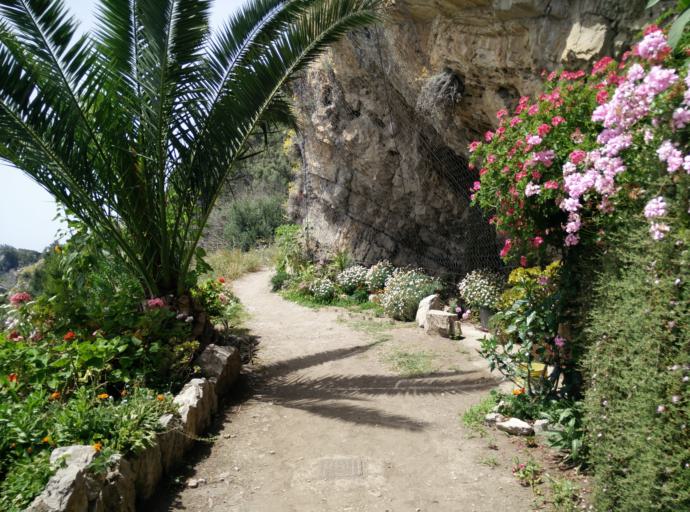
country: IT
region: Campania
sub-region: Provincia di Napoli
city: Massa Lubrense
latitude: 40.5810
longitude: 14.3466
